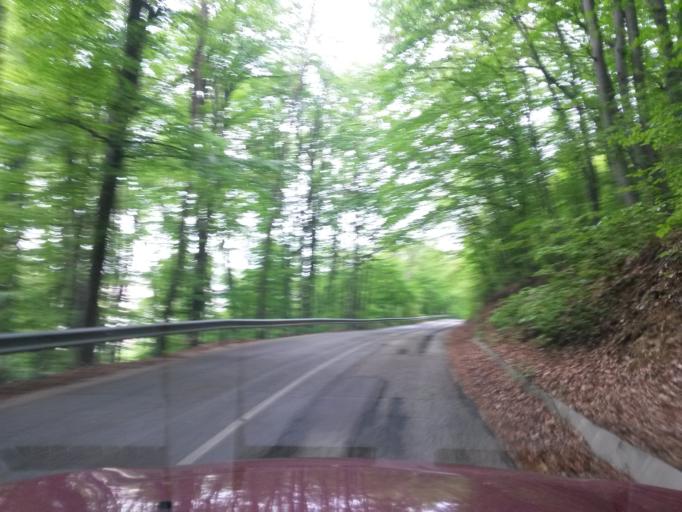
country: SK
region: Kosicky
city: Roznava
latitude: 48.5646
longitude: 20.4722
